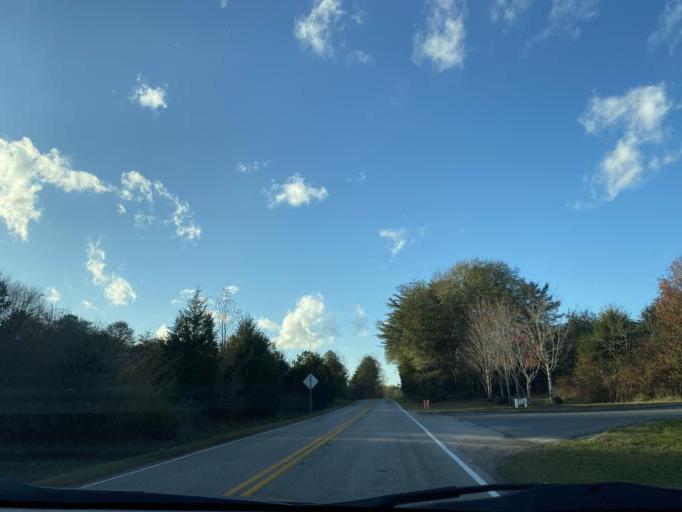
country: US
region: South Carolina
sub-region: York County
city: Clover
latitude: 35.1272
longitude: -81.2216
